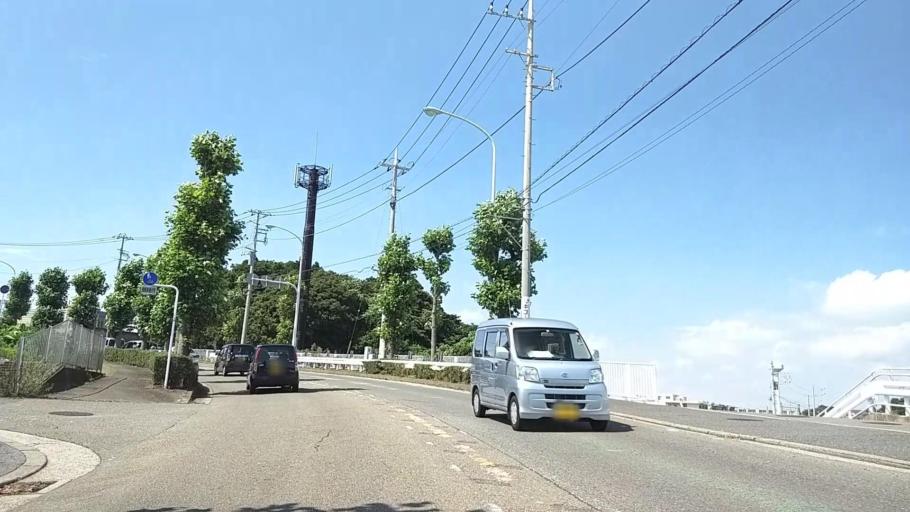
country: JP
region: Kanagawa
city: Fujisawa
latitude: 35.3674
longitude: 139.5021
